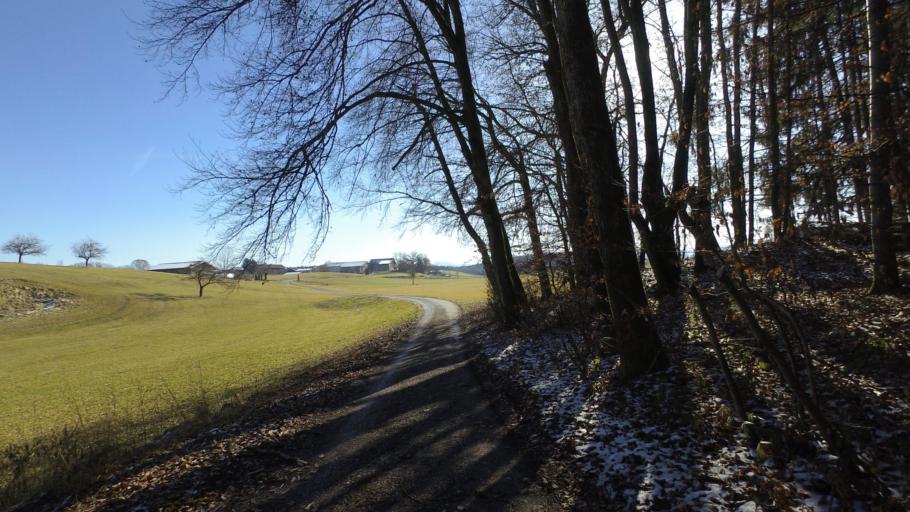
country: DE
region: Bavaria
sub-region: Upper Bavaria
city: Chieming
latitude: 47.9218
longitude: 12.5619
